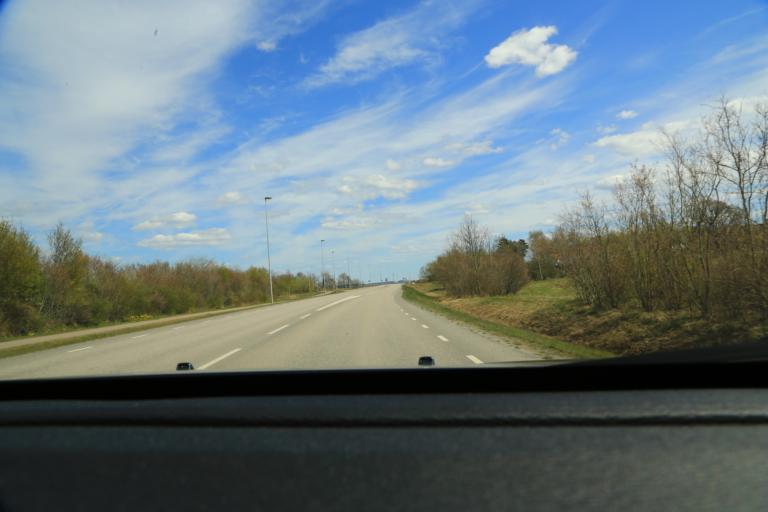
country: SE
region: Halland
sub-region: Varbergs Kommun
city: Varberg
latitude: 57.1110
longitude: 12.2980
